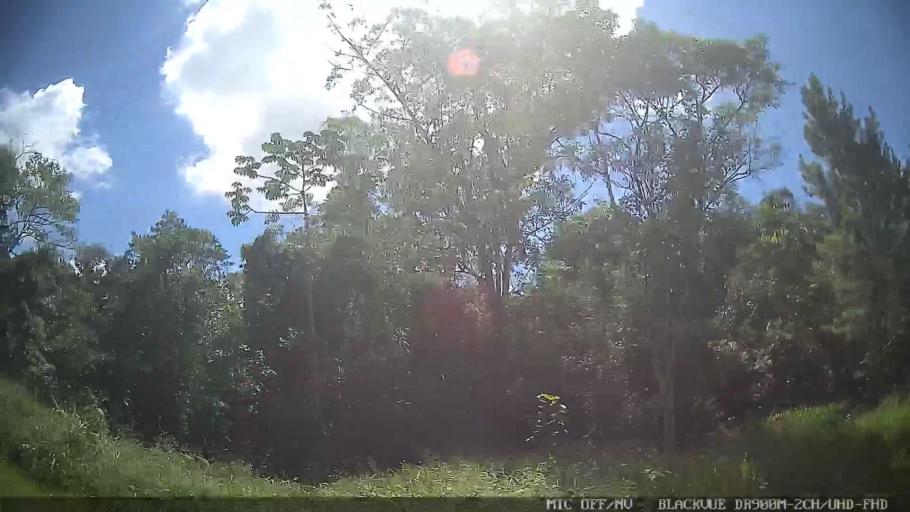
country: BR
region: Sao Paulo
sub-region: Mogi das Cruzes
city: Mogi das Cruzes
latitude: -23.6690
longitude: -46.2099
